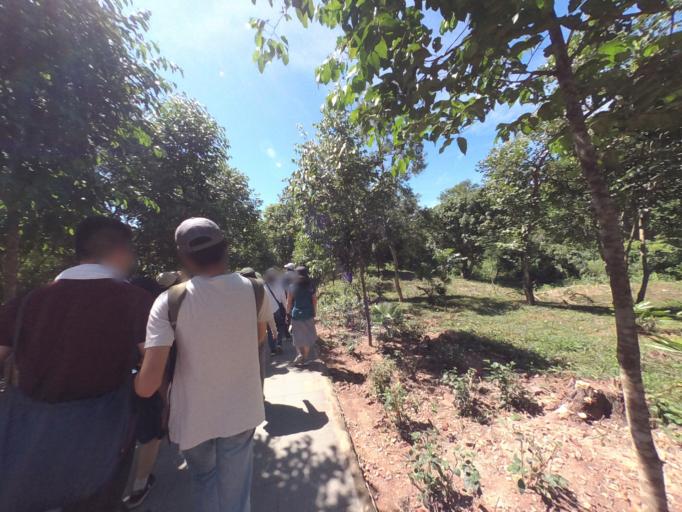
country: VN
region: Quang Nam
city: Dai Loc
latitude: 15.7665
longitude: 108.1223
